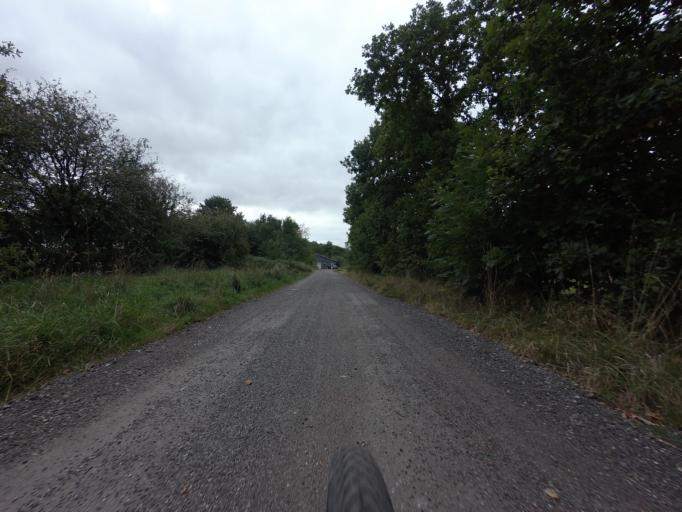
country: DK
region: Central Jutland
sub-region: Ikast-Brande Kommune
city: Brande
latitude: 55.8730
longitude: 9.0334
